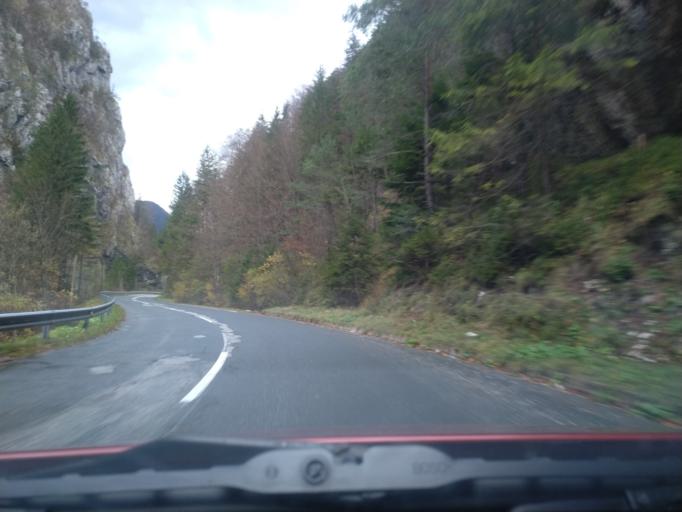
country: SI
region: Luce
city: Luce
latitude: 46.3815
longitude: 14.7273
